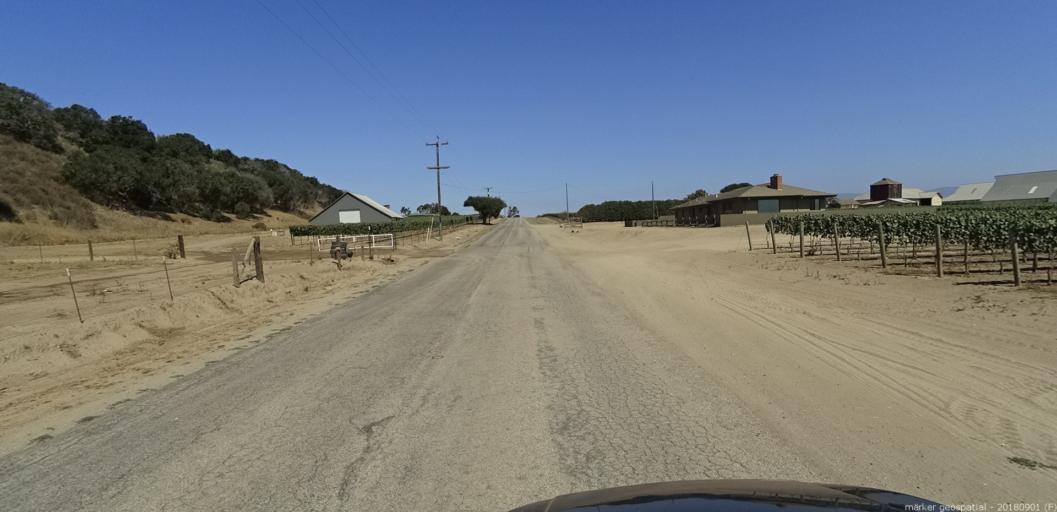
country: US
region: California
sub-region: Monterey County
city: Chualar
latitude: 36.5157
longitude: -121.5189
